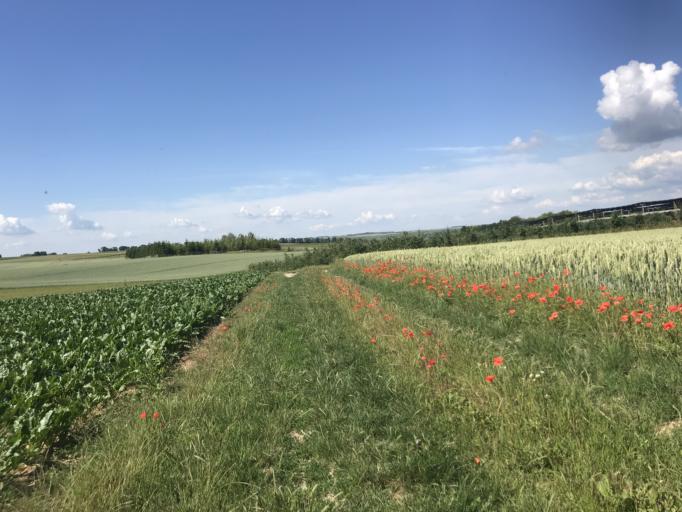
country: DE
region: Rheinland-Pfalz
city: Stadecken-Elsheim
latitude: 49.9400
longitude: 8.1266
